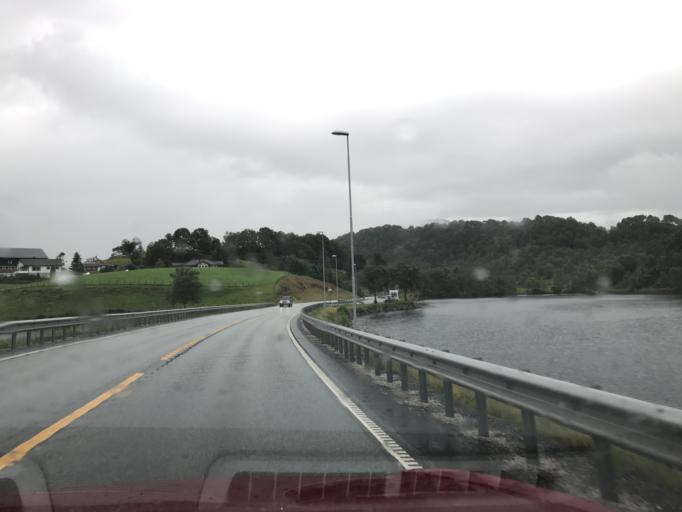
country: NO
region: Rogaland
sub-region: Bjerkreim
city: Vikesa
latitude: 58.5519
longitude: 6.0673
